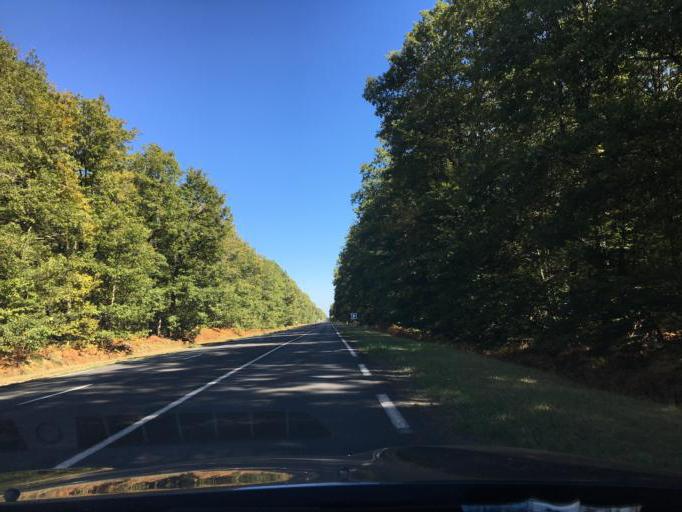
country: FR
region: Centre
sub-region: Departement d'Indre-et-Loire
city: Cheille
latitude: 47.2314
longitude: 0.4016
